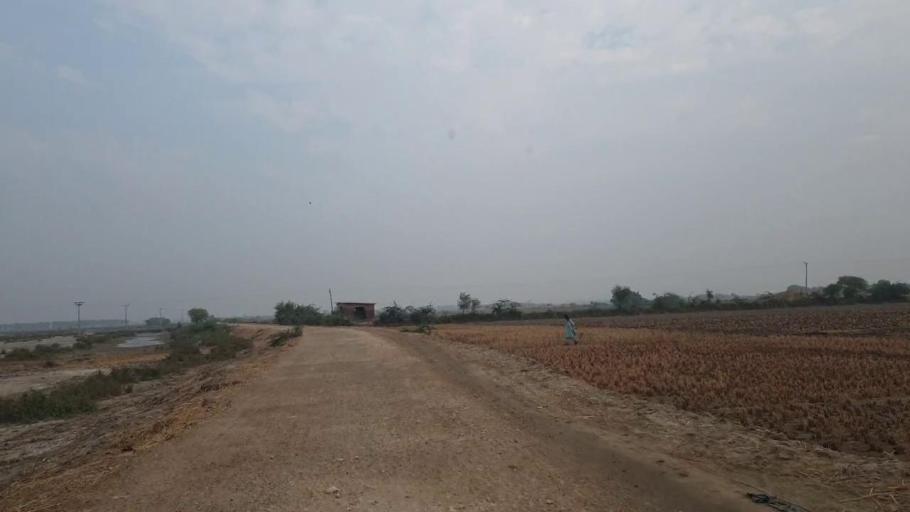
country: PK
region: Sindh
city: Talhar
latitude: 24.8140
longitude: 68.8764
